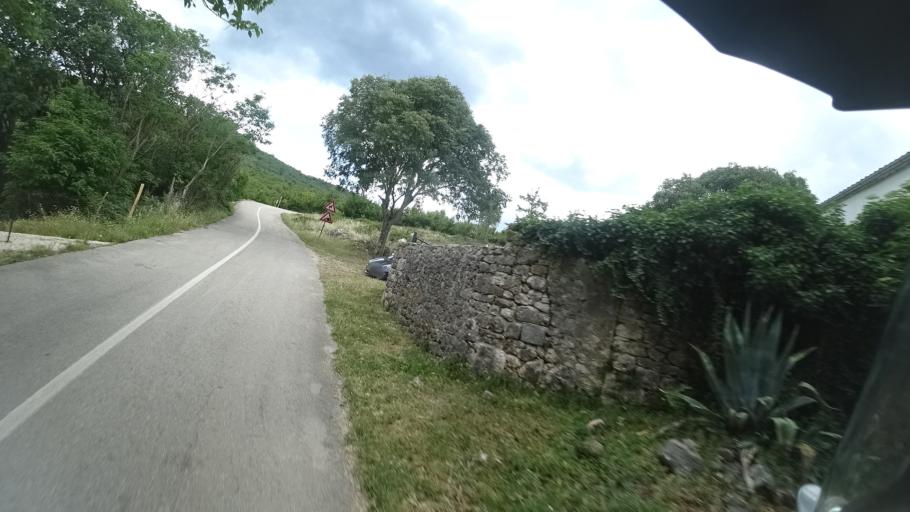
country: HR
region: Zadarska
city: Gracac
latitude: 44.1921
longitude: 15.8870
